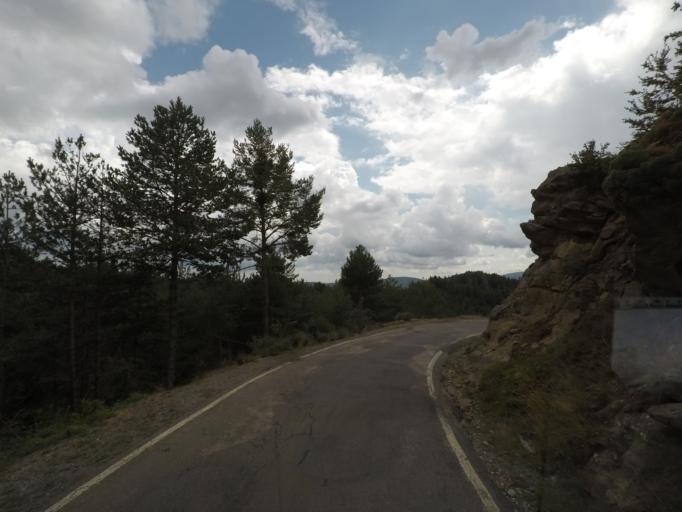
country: ES
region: Aragon
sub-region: Provincia de Huesca
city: Boltana
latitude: 42.4006
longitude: -0.0304
